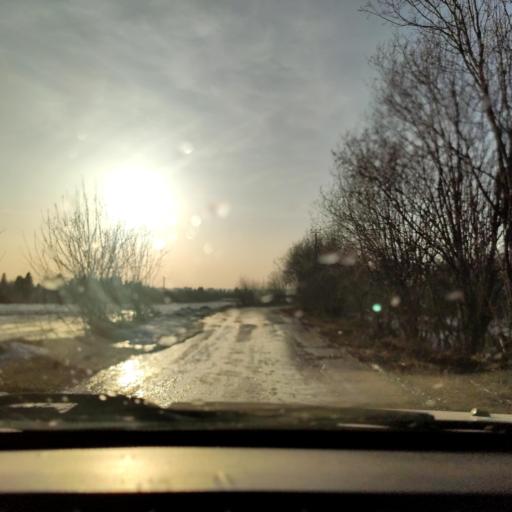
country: RU
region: Perm
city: Novyye Lyady
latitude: 58.1471
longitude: 56.5046
